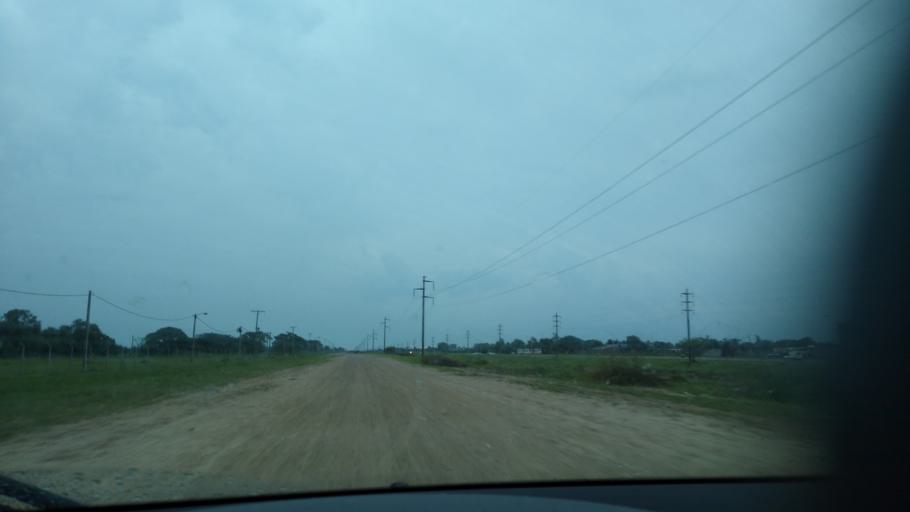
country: AR
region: Chaco
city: Puerto Vilelas
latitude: -27.5009
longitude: -58.9749
